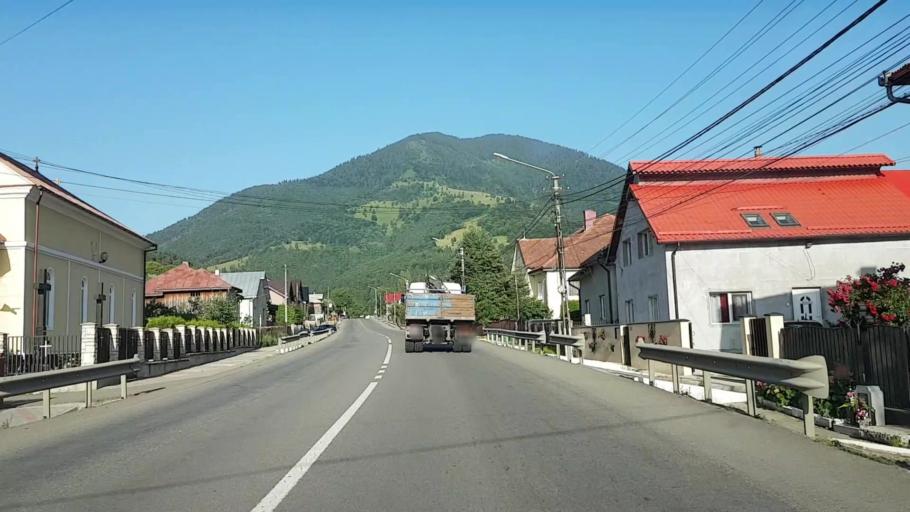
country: RO
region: Bistrita-Nasaud
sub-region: Comuna Tiha Bargaului
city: Tureac
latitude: 47.2102
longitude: 24.8593
